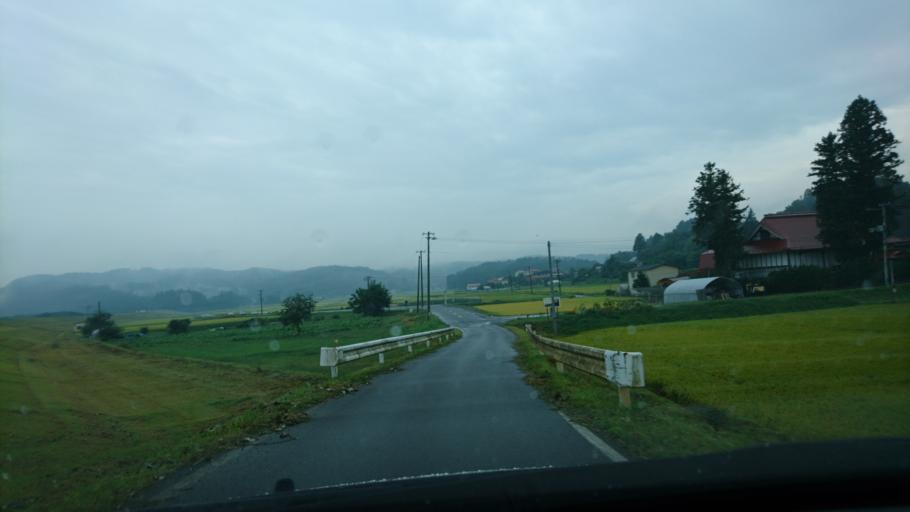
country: JP
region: Iwate
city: Ichinoseki
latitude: 38.8909
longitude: 141.2612
